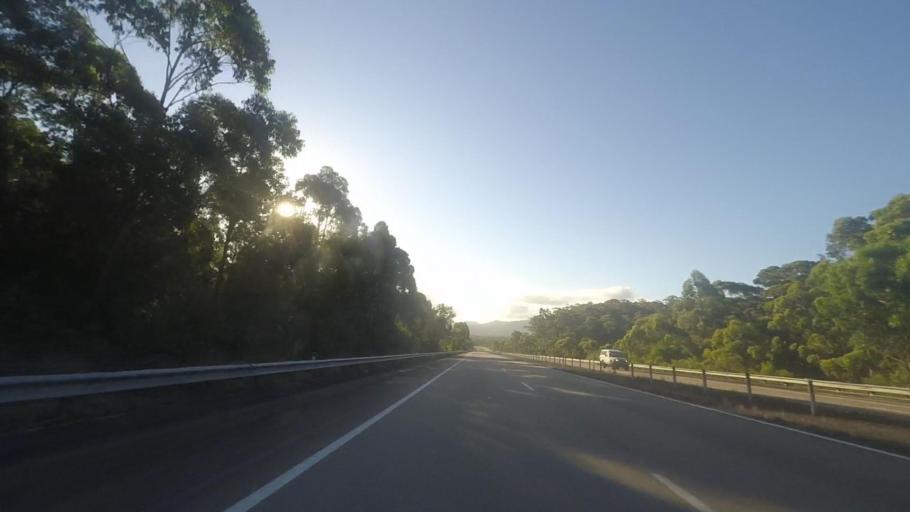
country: AU
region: New South Wales
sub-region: Great Lakes
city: Bulahdelah
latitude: -32.3877
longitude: 152.2446
